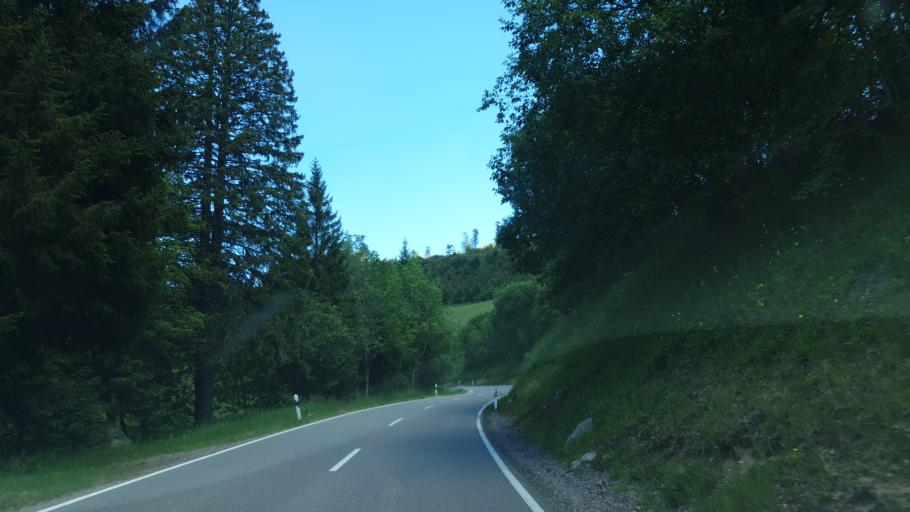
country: DE
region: Baden-Wuerttemberg
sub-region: Freiburg Region
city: Todtnau
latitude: 47.8599
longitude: 7.9185
